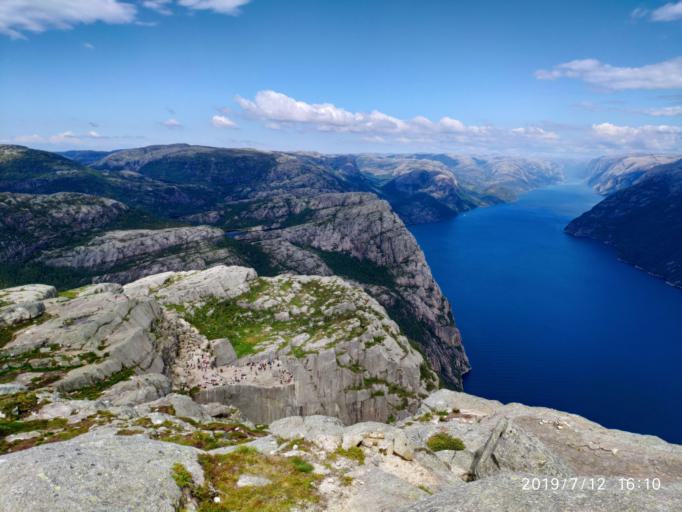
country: NO
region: Rogaland
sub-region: Forsand
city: Forsand
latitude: 58.9852
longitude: 6.1866
